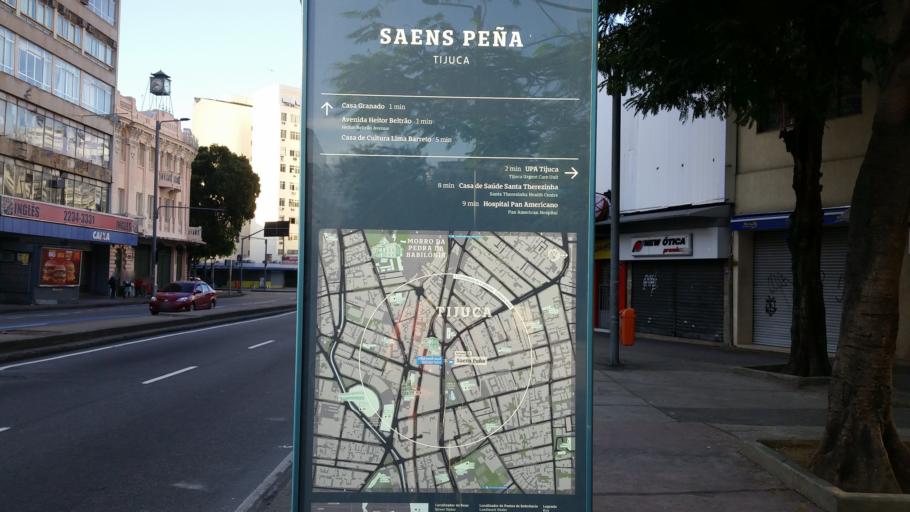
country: BR
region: Rio de Janeiro
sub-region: Rio De Janeiro
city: Rio de Janeiro
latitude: -22.9236
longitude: -43.2317
